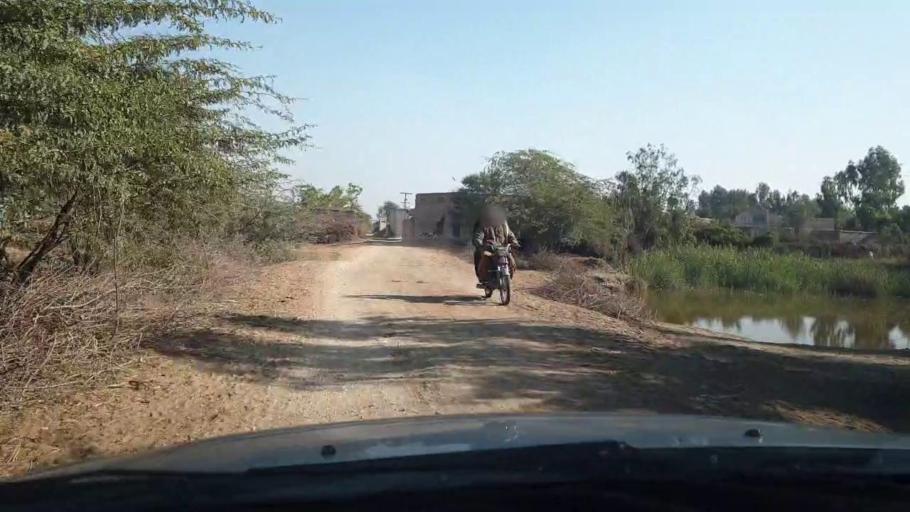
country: PK
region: Sindh
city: Mirpur Mathelo
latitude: 27.9760
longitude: 69.5491
